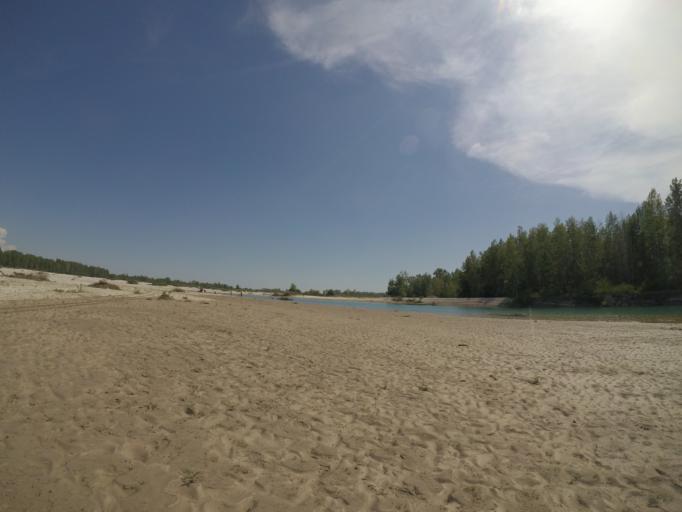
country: IT
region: Friuli Venezia Giulia
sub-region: Provincia di Udine
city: Camino al Tagliamento
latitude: 45.9072
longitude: 12.9214
